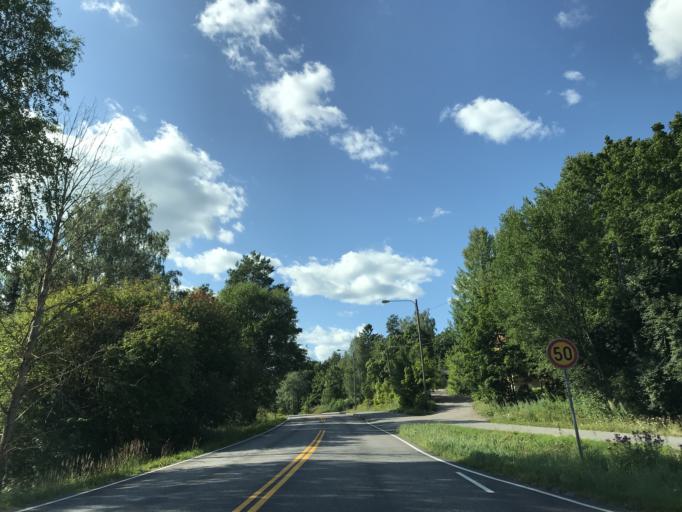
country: FI
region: Uusimaa
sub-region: Helsinki
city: Nurmijaervi
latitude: 60.4219
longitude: 24.8671
